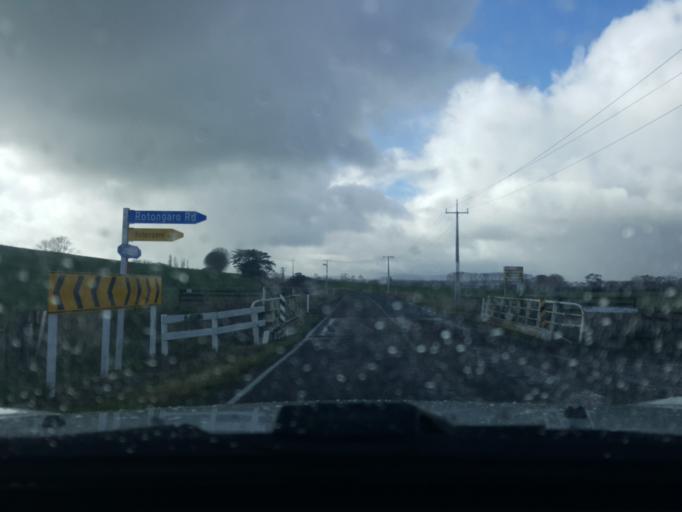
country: NZ
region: Waikato
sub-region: Waikato District
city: Te Kauwhata
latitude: -37.4489
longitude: 175.1022
